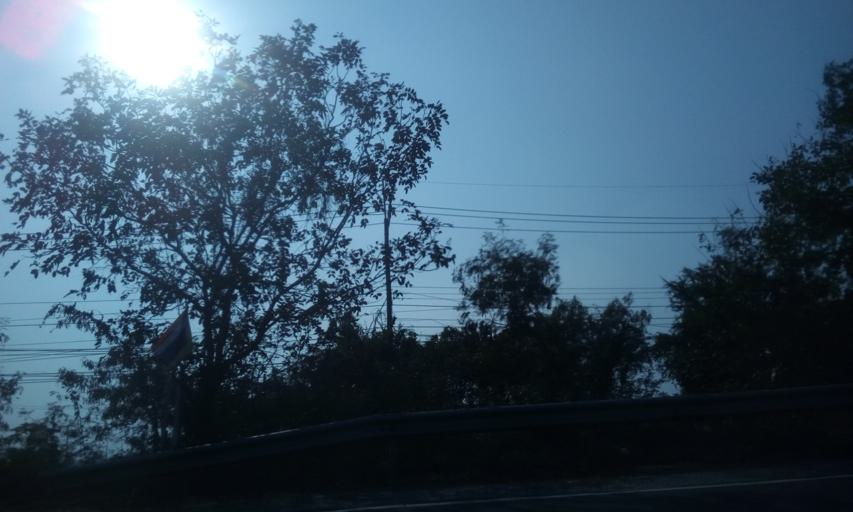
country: TH
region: Sing Buri
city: Phrom Buri
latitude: 14.7797
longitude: 100.4339
